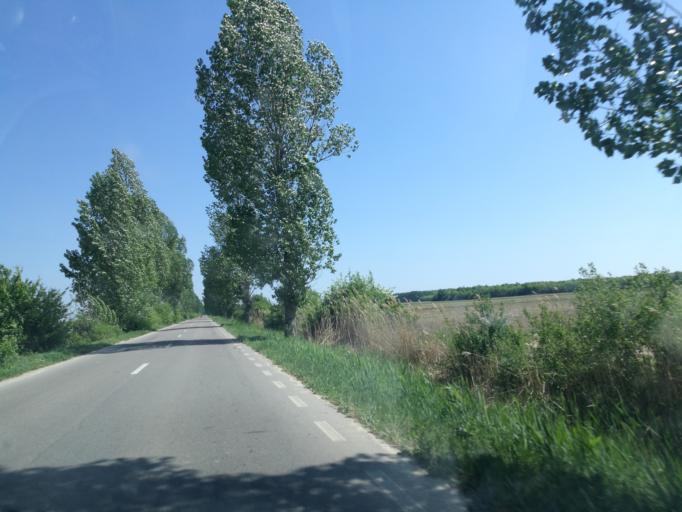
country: RO
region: Ialomita
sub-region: Comuna Adancata
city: Adancata
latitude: 44.7526
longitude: 26.4253
